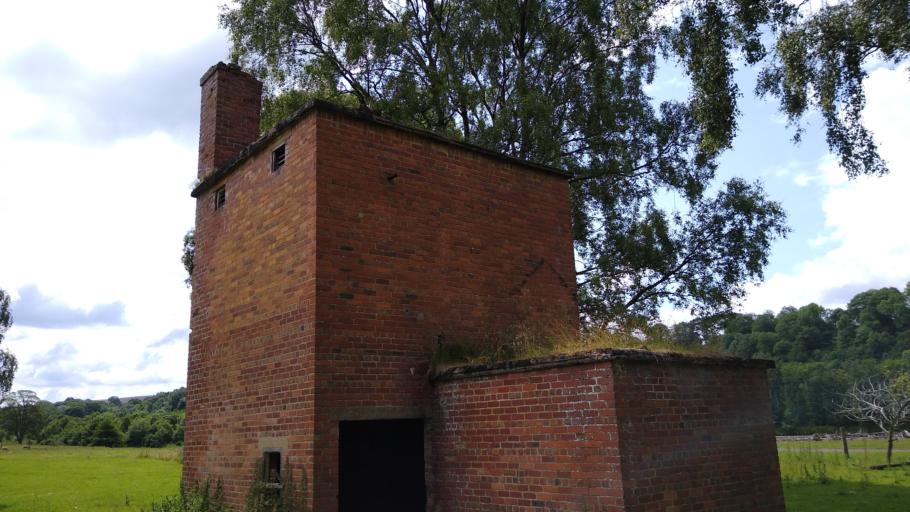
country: GB
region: England
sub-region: Northumberland
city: Greenhead
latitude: 54.9360
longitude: -2.5112
